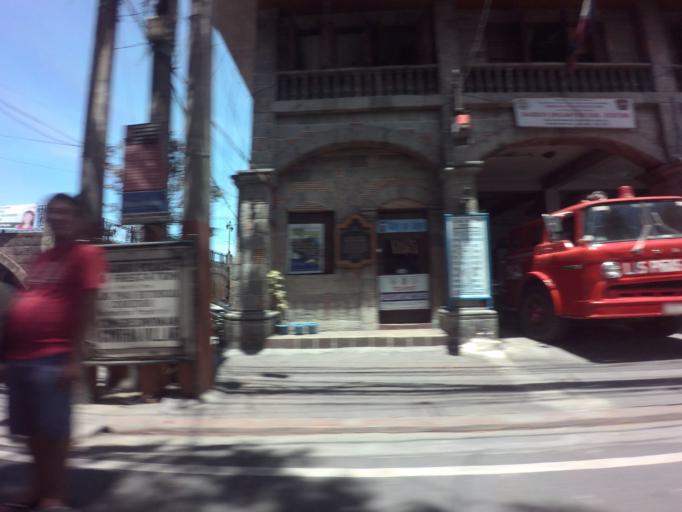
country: PH
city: Sambayanihan People's Village
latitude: 14.4808
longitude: 120.9815
